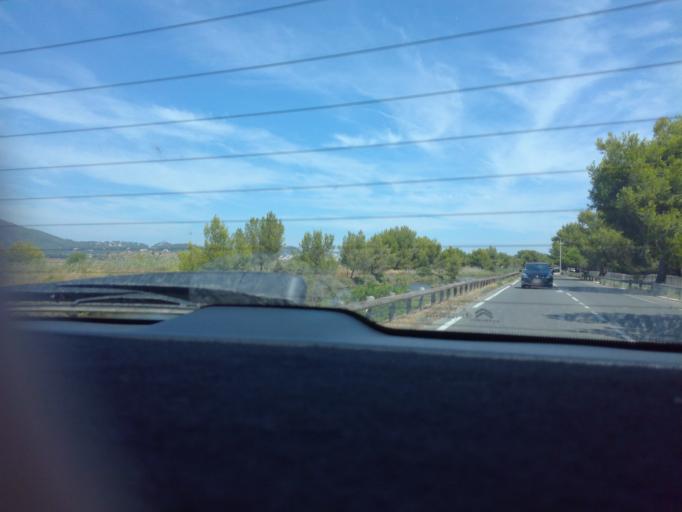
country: FR
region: Provence-Alpes-Cote d'Azur
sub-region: Departement du Var
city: Hyeres
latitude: 43.0703
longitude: 6.1473
